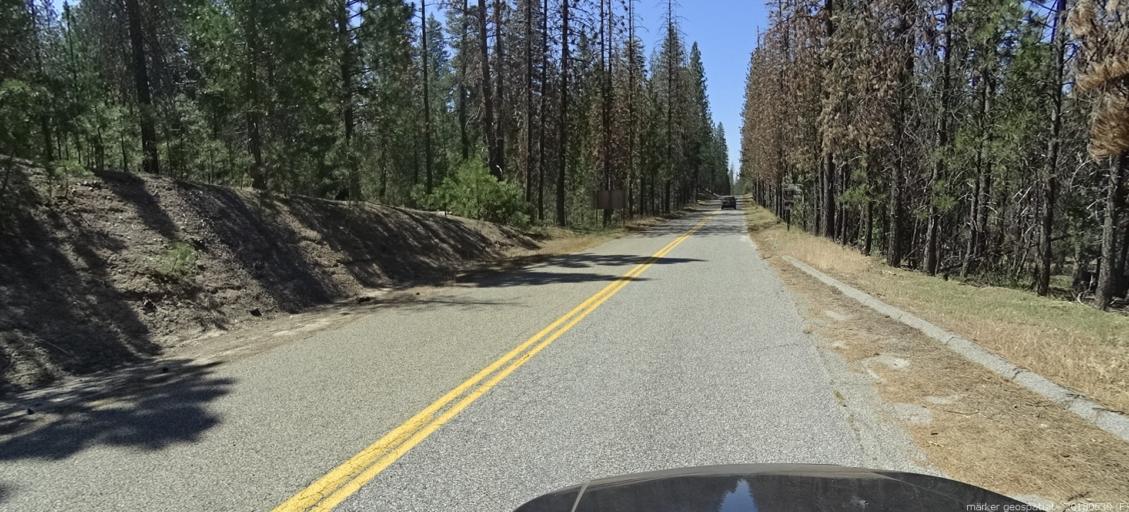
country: US
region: California
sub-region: Madera County
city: Oakhurst
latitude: 37.4114
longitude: -119.3473
